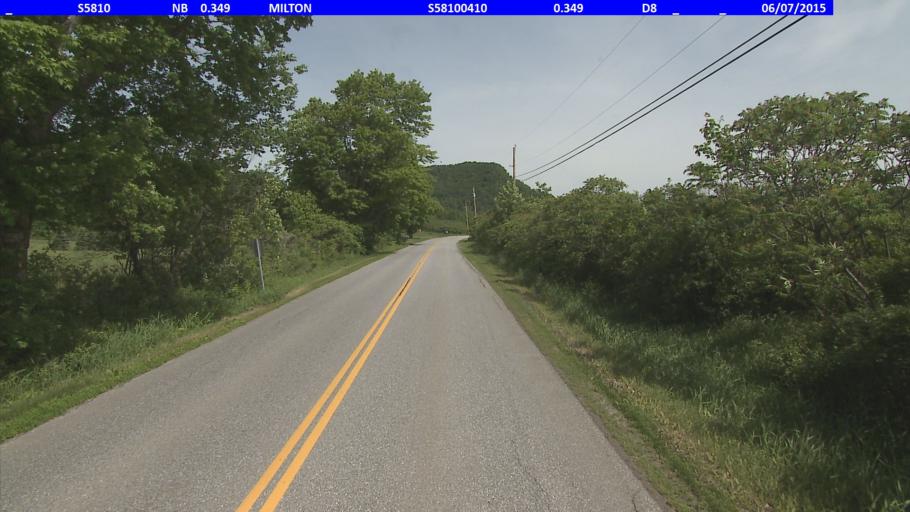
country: US
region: Vermont
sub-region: Chittenden County
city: Colchester
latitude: 44.5869
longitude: -73.1301
